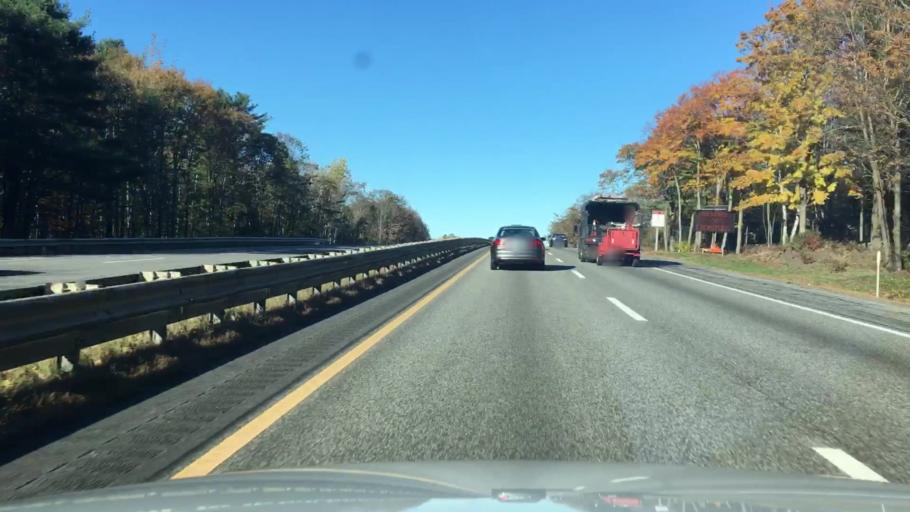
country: US
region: Maine
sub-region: Cumberland County
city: Freeport
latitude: 43.8536
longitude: -70.1138
